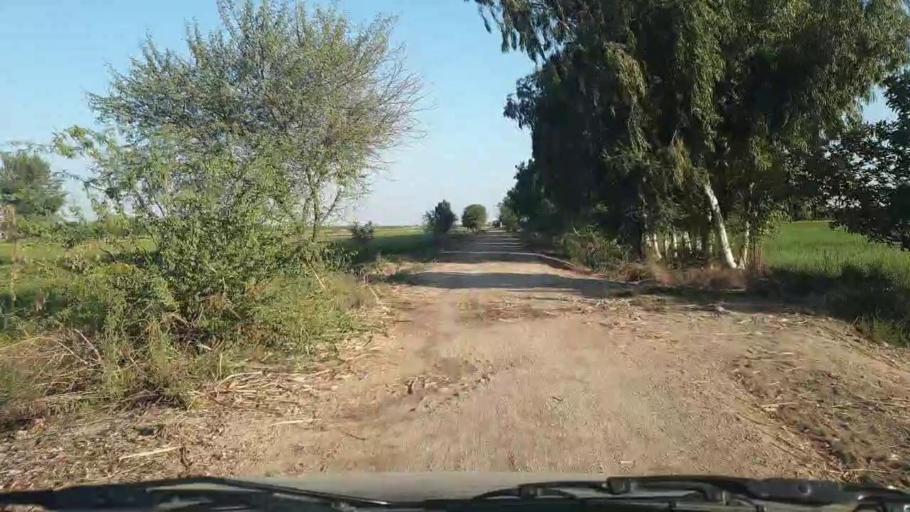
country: PK
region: Sindh
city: Samaro
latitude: 25.3398
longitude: 69.3134
